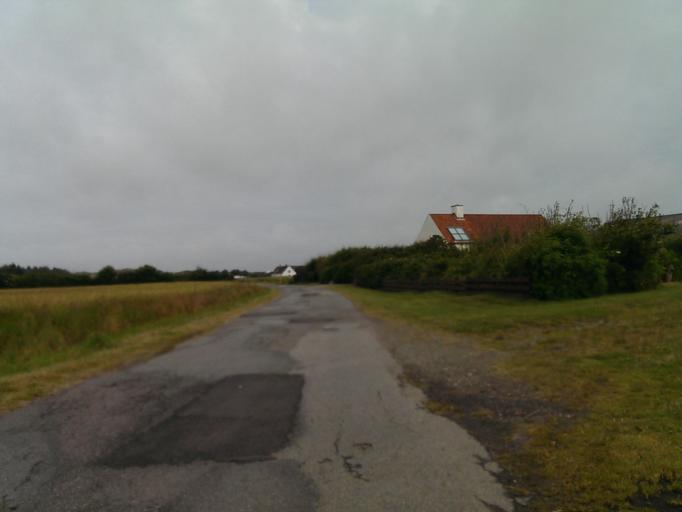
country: DK
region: North Denmark
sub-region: Jammerbugt Kommune
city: Pandrup
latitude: 57.3797
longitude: 9.7327
